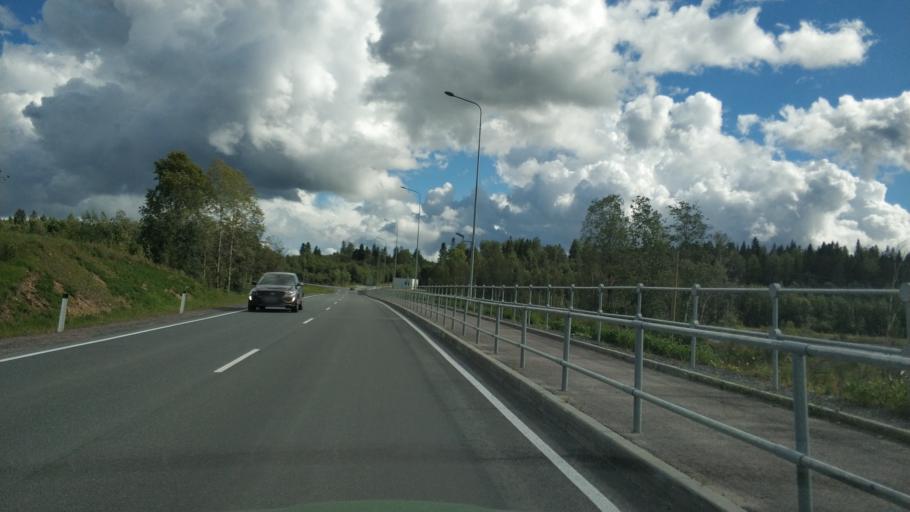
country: RU
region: Republic of Karelia
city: Ruskeala
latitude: 61.9473
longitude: 30.5933
